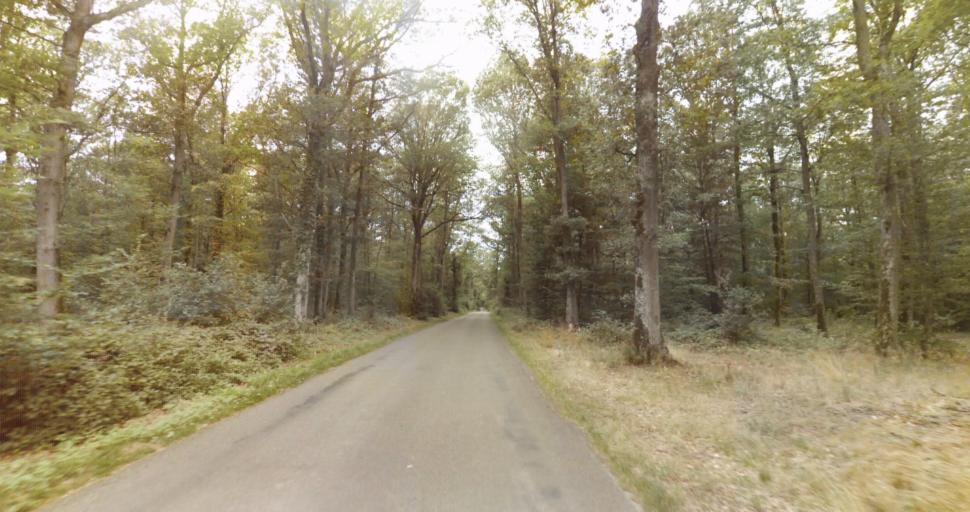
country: FR
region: Haute-Normandie
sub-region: Departement de l'Eure
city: Marcilly-sur-Eure
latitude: 48.8681
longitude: 1.3393
